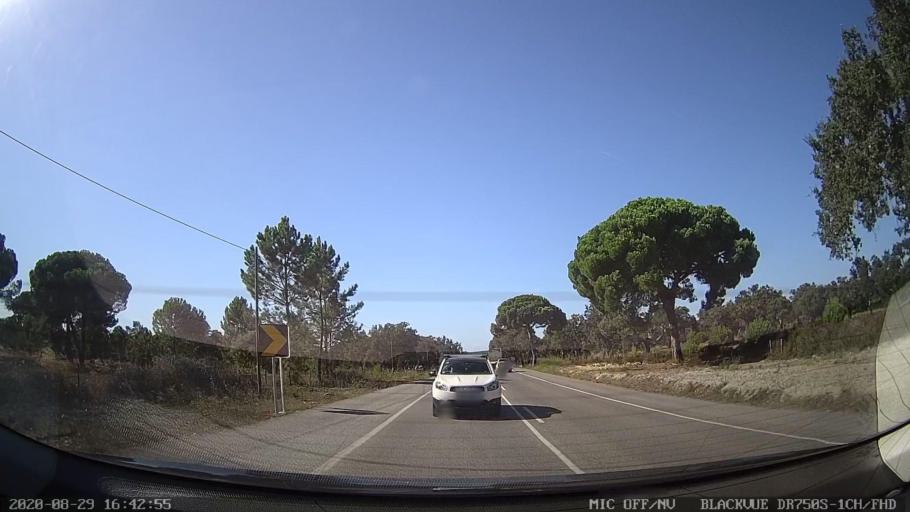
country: PT
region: Setubal
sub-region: Alcacer do Sal
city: Alcacer do Sal
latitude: 38.5398
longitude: -8.6427
